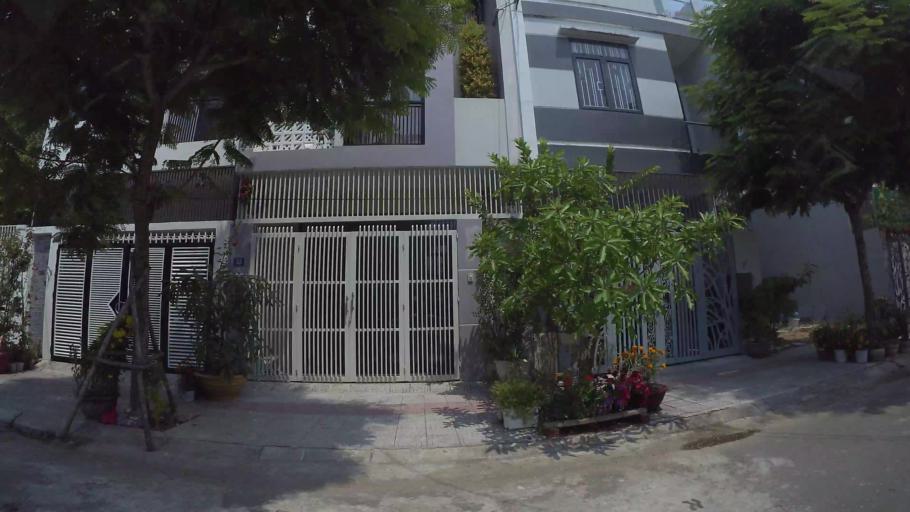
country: VN
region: Da Nang
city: Cam Le
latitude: 16.0212
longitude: 108.2249
